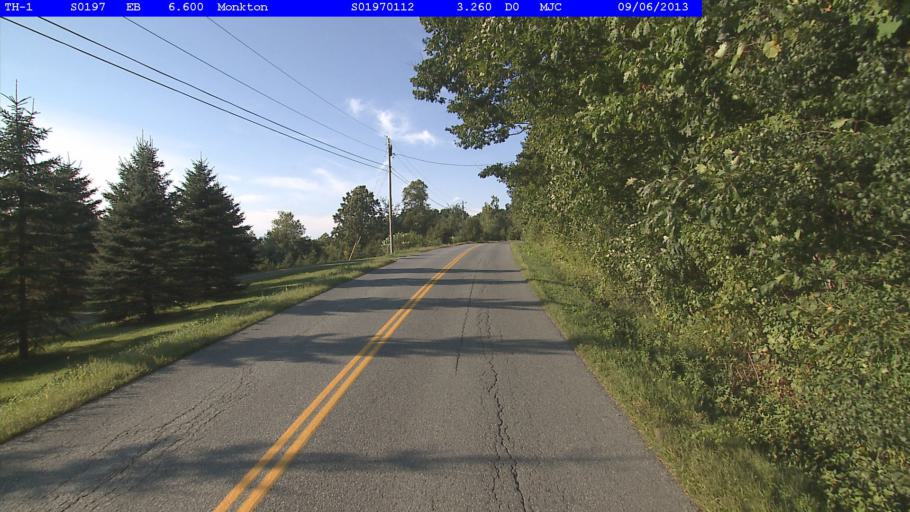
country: US
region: Vermont
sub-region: Chittenden County
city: Hinesburg
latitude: 44.2242
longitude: -73.1534
